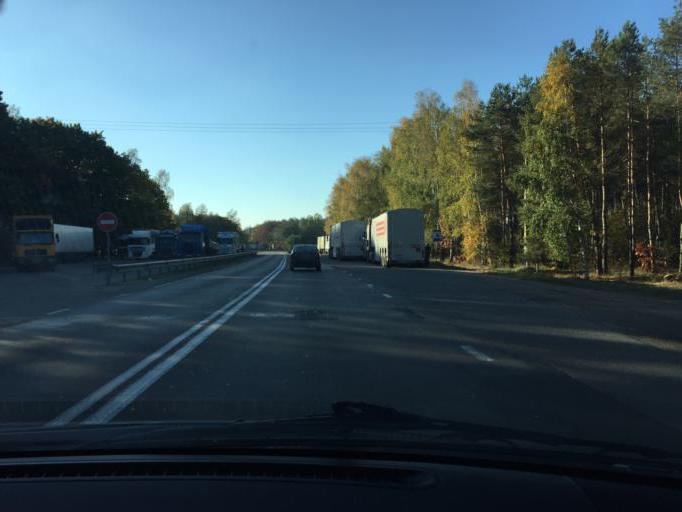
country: BY
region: Brest
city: Luninyets
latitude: 52.2769
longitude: 26.9598
